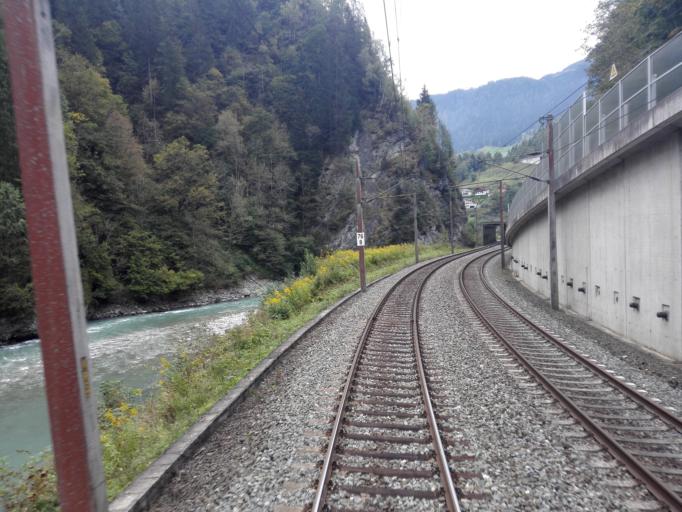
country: AT
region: Salzburg
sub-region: Politischer Bezirk Zell am See
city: Lend
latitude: 47.3039
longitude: 13.0348
